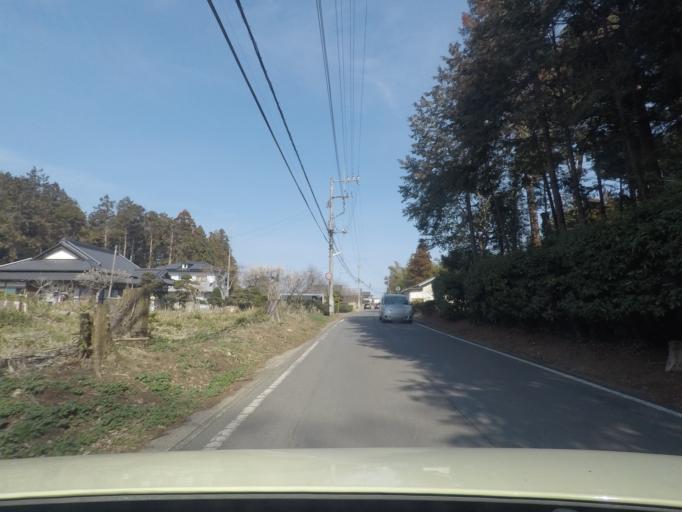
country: JP
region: Ibaraki
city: Ishioka
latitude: 36.1931
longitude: 140.3131
